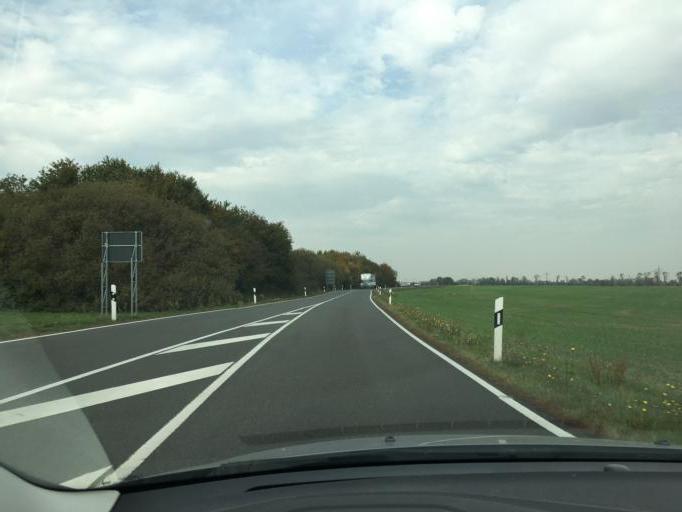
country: DE
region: Saxony
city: Zwochau
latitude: 51.4405
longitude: 12.2747
